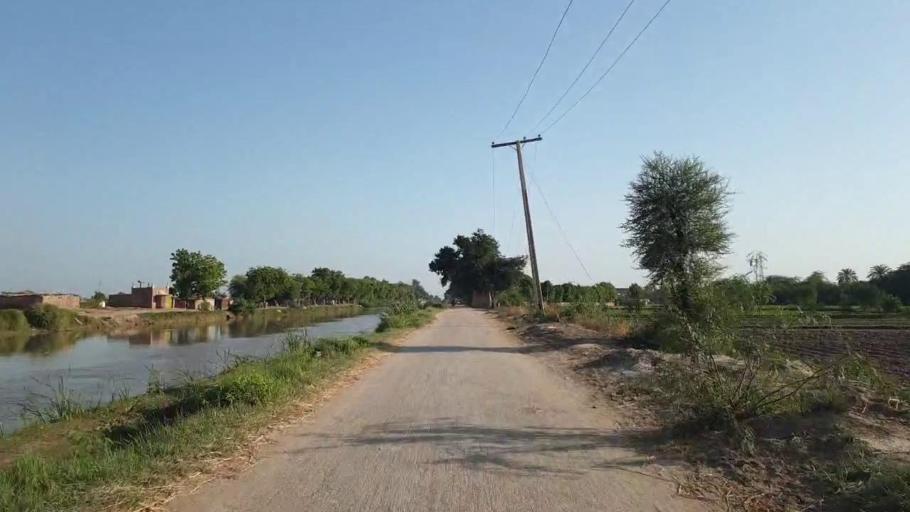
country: PK
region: Sindh
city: Hyderabad
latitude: 25.3213
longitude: 68.4275
